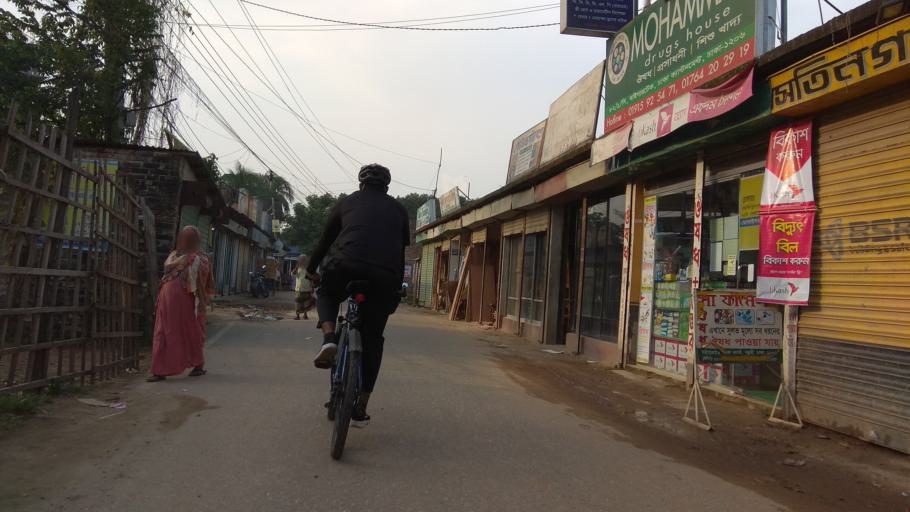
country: BD
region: Dhaka
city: Tungi
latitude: 23.8333
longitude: 90.3889
